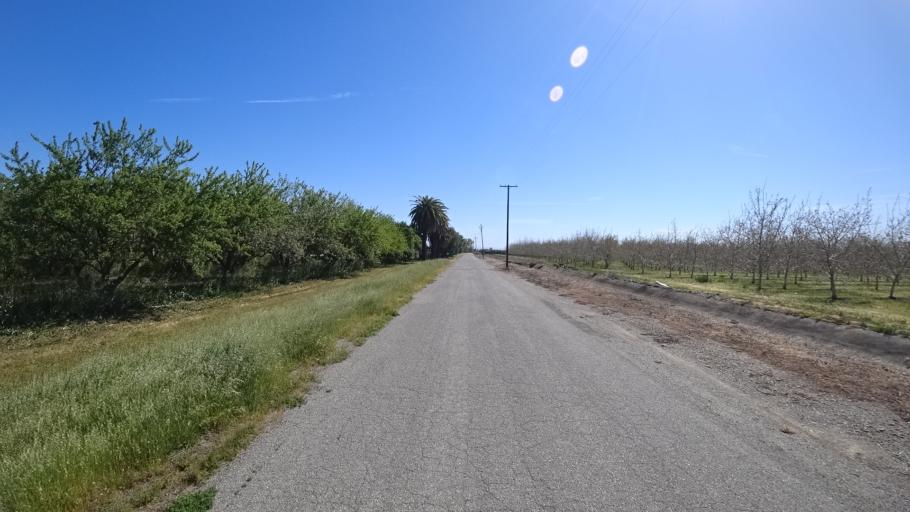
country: US
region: California
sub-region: Glenn County
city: Orland
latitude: 39.7431
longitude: -122.1188
